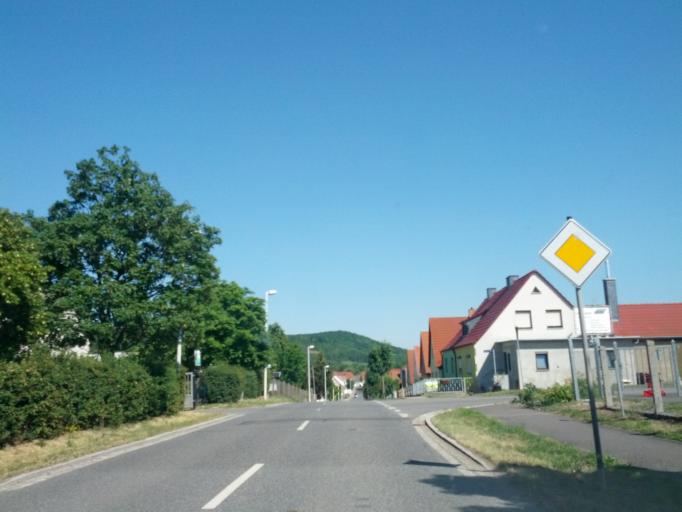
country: DE
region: Thuringia
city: Wandersleben
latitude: 50.8692
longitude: 10.8170
